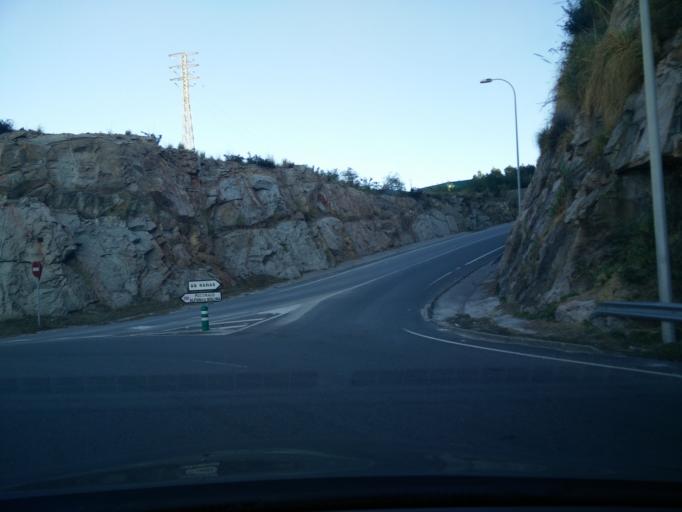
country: ES
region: Galicia
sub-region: Provincia da Coruna
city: A Coruna
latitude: 43.3403
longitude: -8.4284
